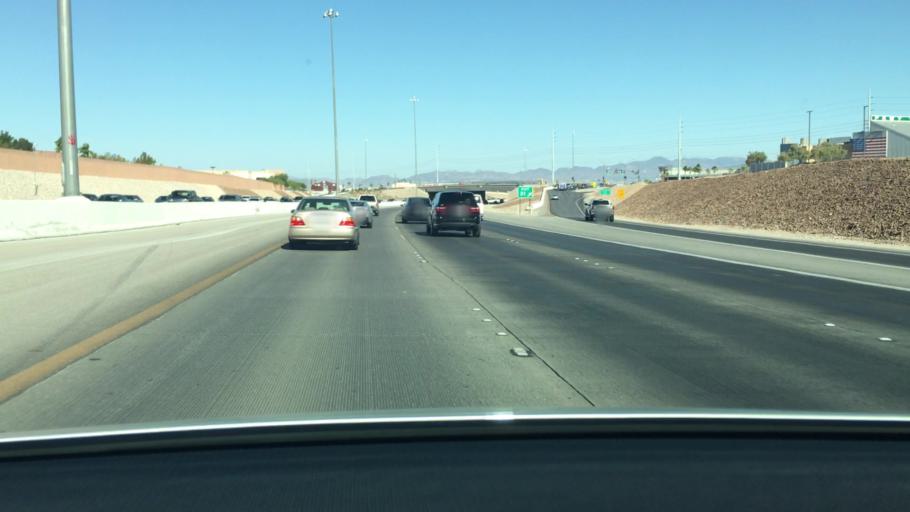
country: US
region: Nevada
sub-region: Clark County
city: Summerlin South
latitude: 36.1174
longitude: -115.3075
